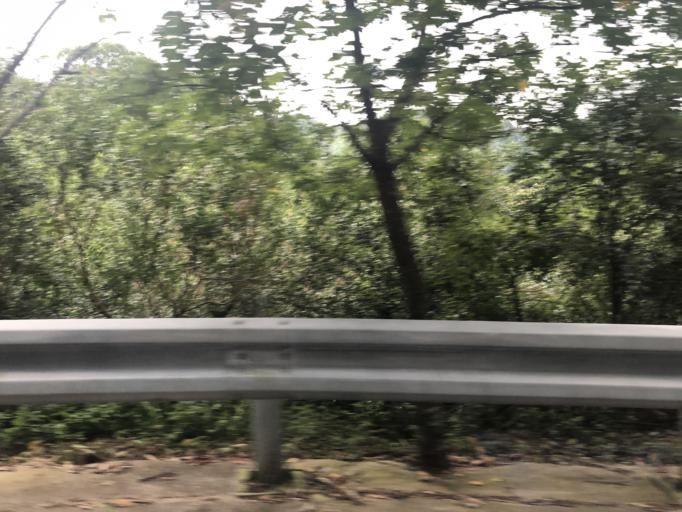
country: TW
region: Taiwan
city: Daxi
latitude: 24.8822
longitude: 121.4186
